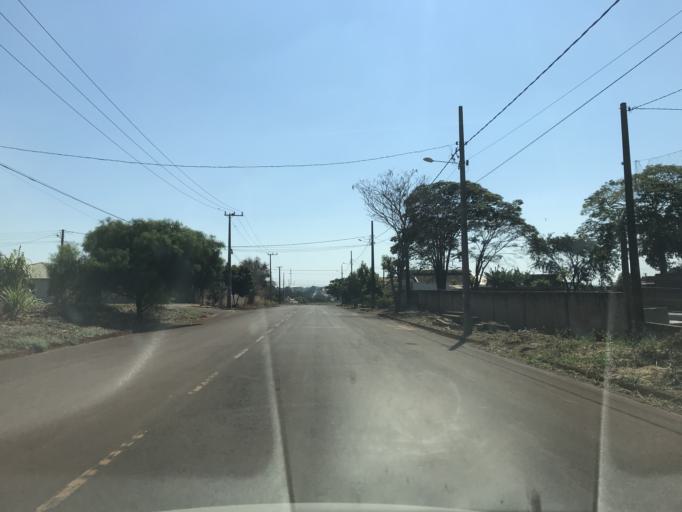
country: BR
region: Parana
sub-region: Palotina
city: Palotina
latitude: -24.2964
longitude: -53.8319
